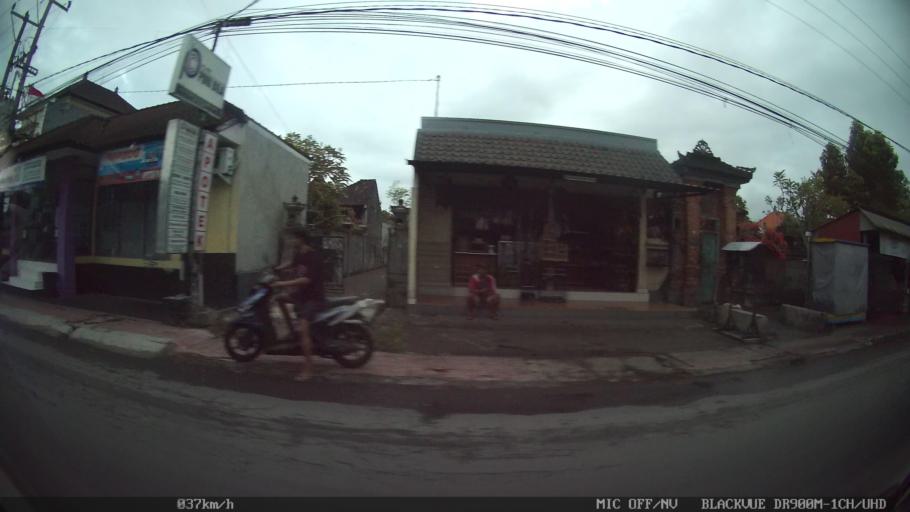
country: ID
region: Bali
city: Banjar Pasekan
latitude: -8.6136
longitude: 115.2836
